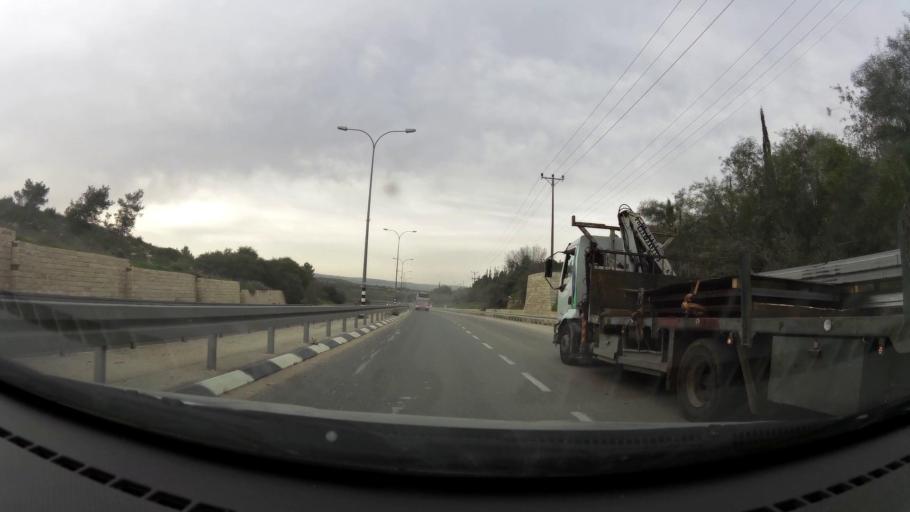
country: IL
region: Jerusalem
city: Bet Shemesh
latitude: 31.6970
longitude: 35.0104
